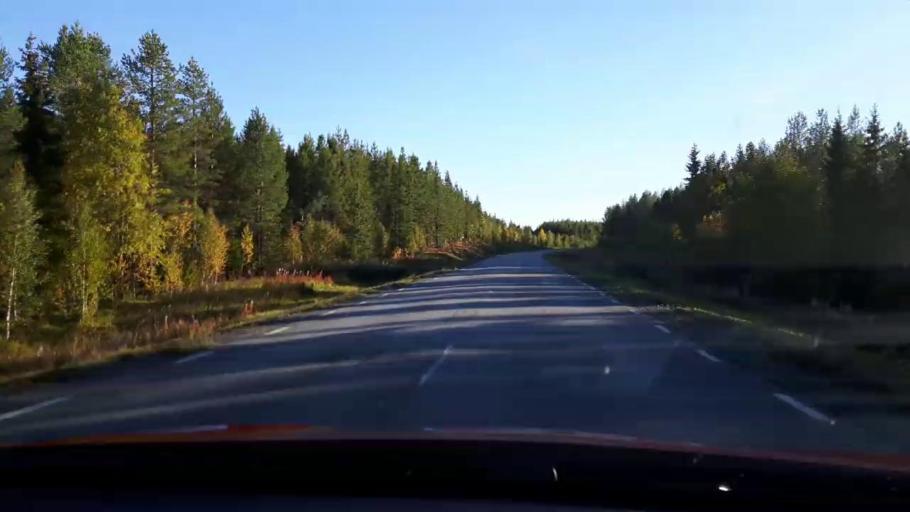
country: SE
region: Jaemtland
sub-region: OEstersunds Kommun
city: Lit
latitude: 63.7633
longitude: 14.7215
